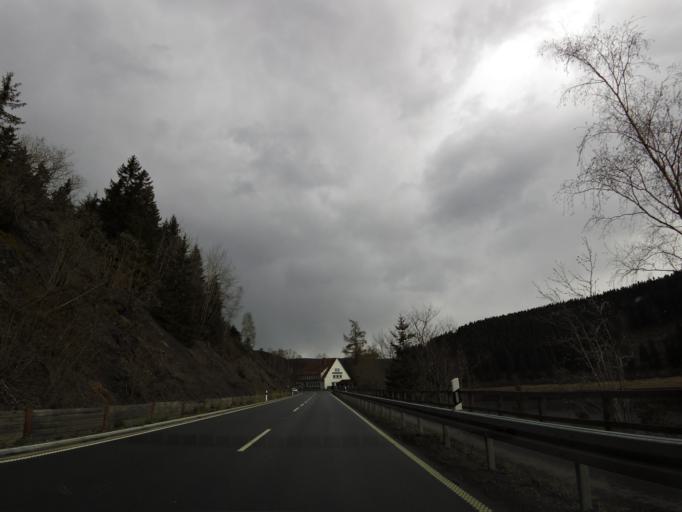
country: DE
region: Lower Saxony
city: Schulenberg im Oberharz
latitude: 51.8296
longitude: 10.4539
